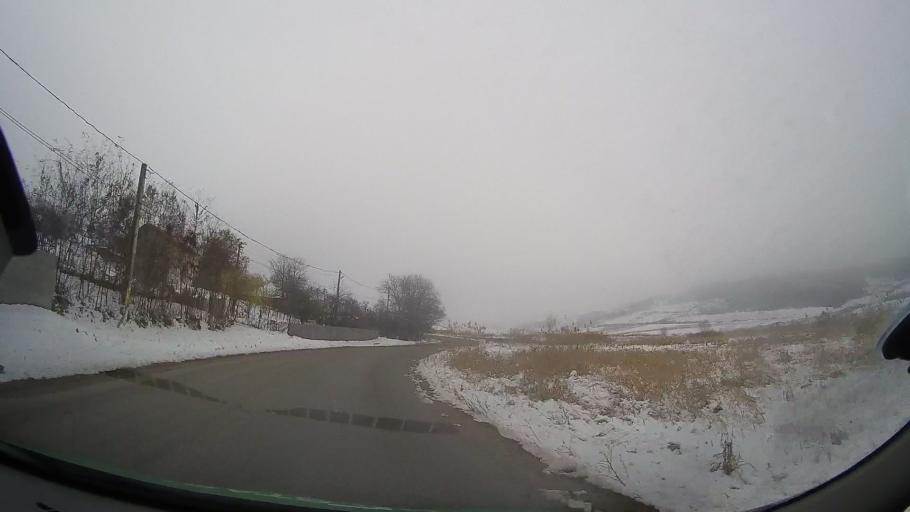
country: RO
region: Bacau
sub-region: Comuna Vultureni
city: Vultureni
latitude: 46.3516
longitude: 27.2888
